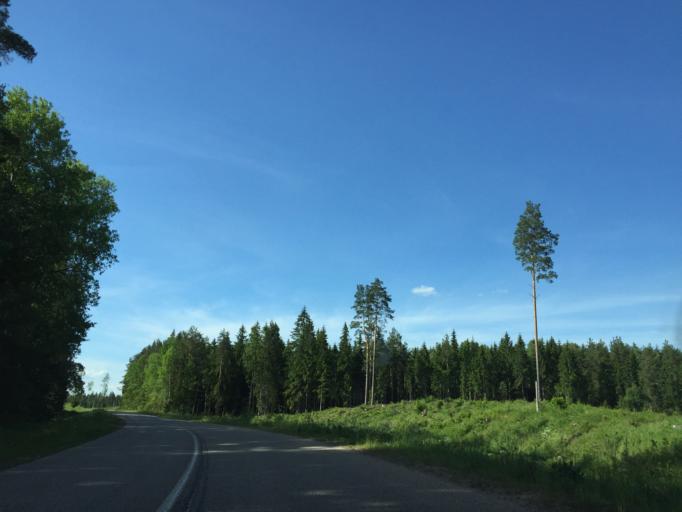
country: LV
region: Rezekne
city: Rezekne
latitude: 56.2861
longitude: 27.2138
